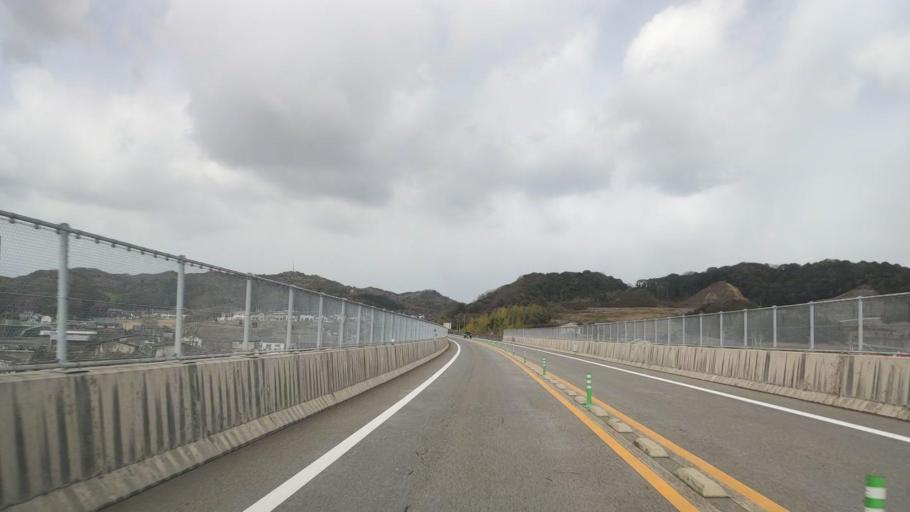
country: JP
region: Ehime
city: Hojo
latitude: 34.0621
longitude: 132.9728
